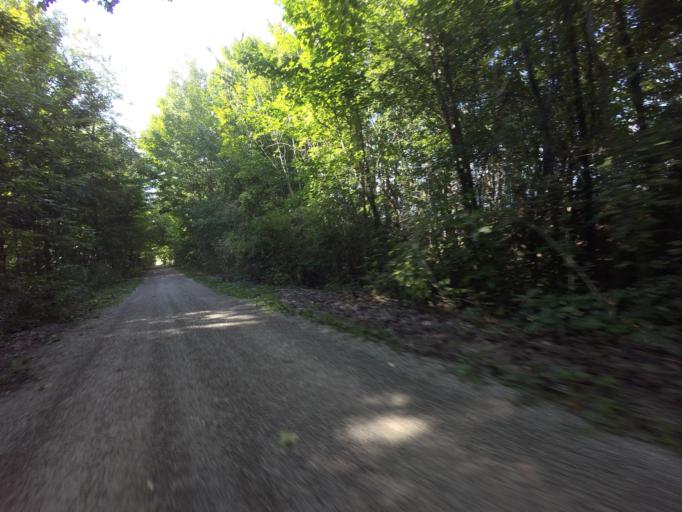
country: CA
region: Ontario
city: Goderich
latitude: 43.7498
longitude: -81.5020
